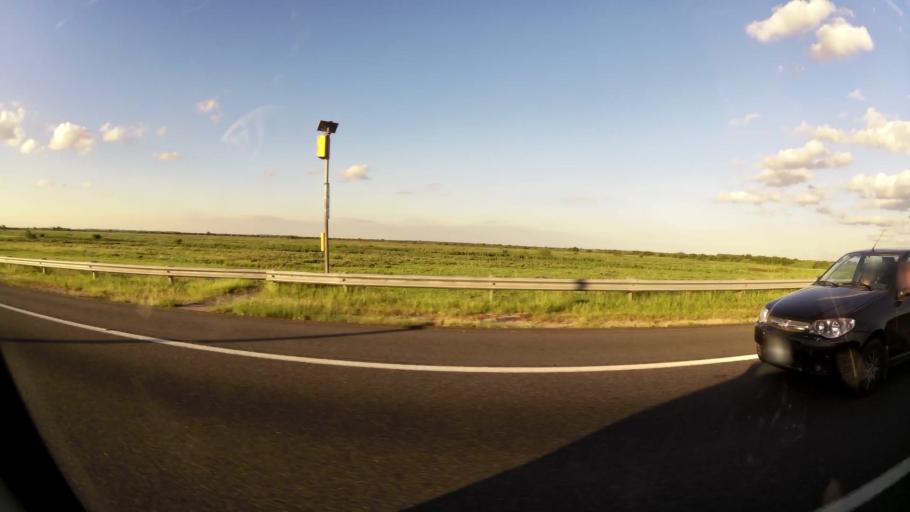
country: AR
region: Buenos Aires
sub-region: Partido de La Plata
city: La Plata
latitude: -34.8440
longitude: -58.0593
